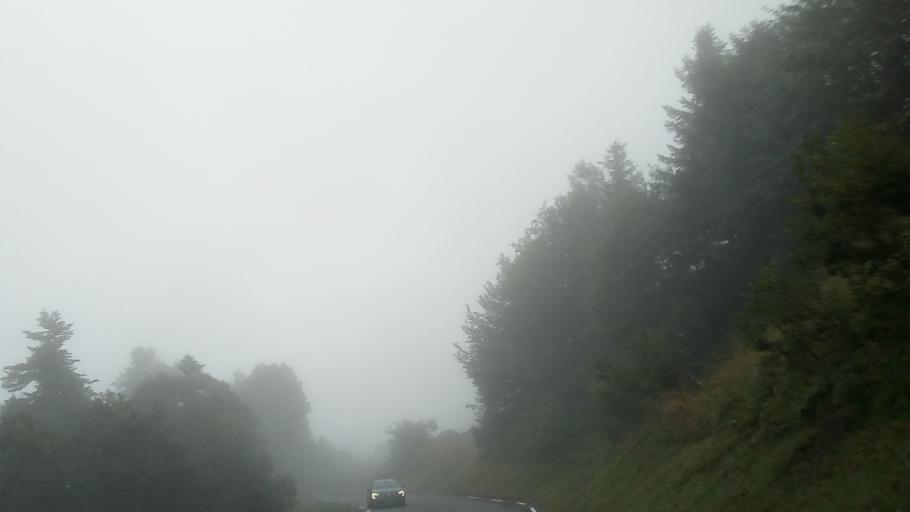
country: FR
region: Midi-Pyrenees
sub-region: Departement des Hautes-Pyrenees
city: Saint-Lary-Soulan
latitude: 42.7837
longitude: 0.1688
